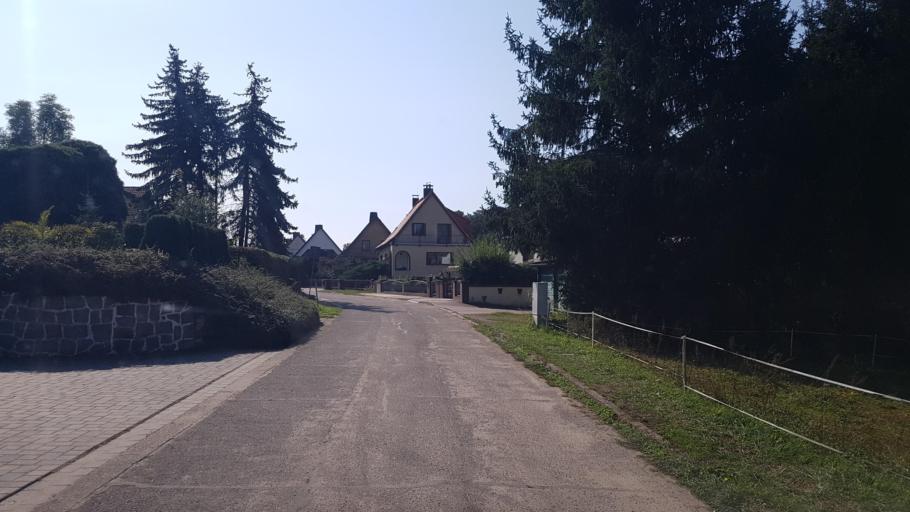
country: DE
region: Brandenburg
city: Vetschau
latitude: 51.7914
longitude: 14.0696
